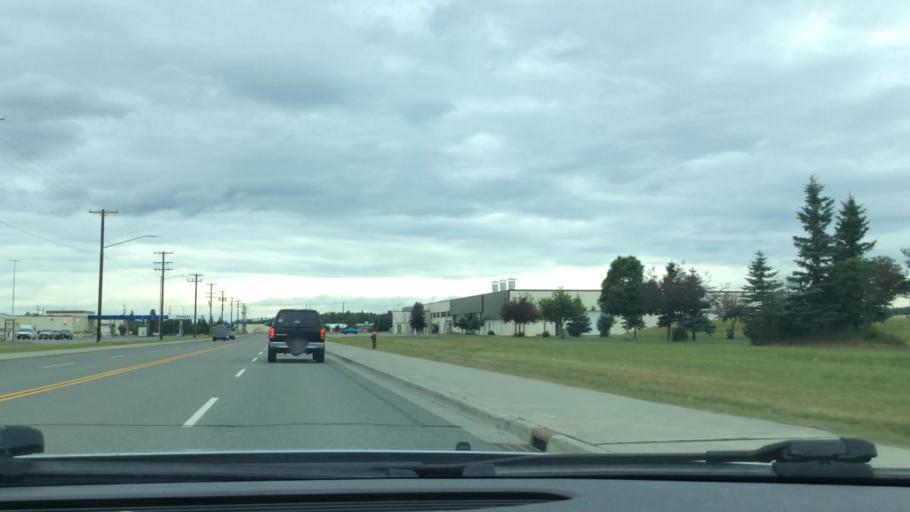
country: US
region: Alaska
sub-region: Anchorage Municipality
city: Anchorage
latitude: 61.2373
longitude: -149.8422
